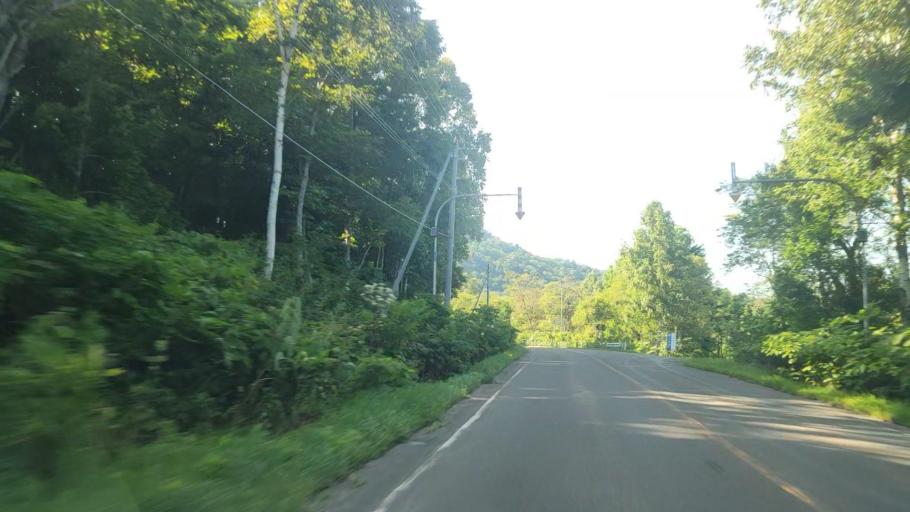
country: JP
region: Hokkaido
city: Nayoro
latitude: 44.7374
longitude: 142.1882
